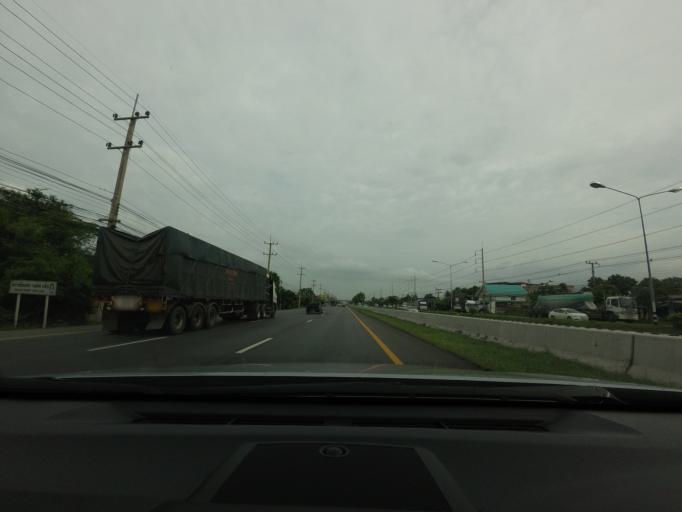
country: TH
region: Phetchaburi
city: Khao Yoi
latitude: 13.2309
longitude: 99.8244
